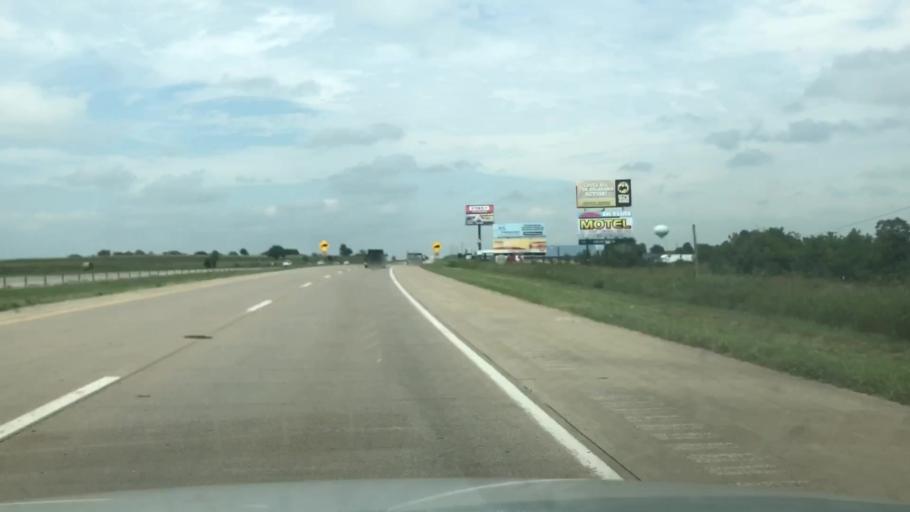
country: US
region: Oklahoma
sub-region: Washington County
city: Bartlesville
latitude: 36.6012
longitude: -95.9353
